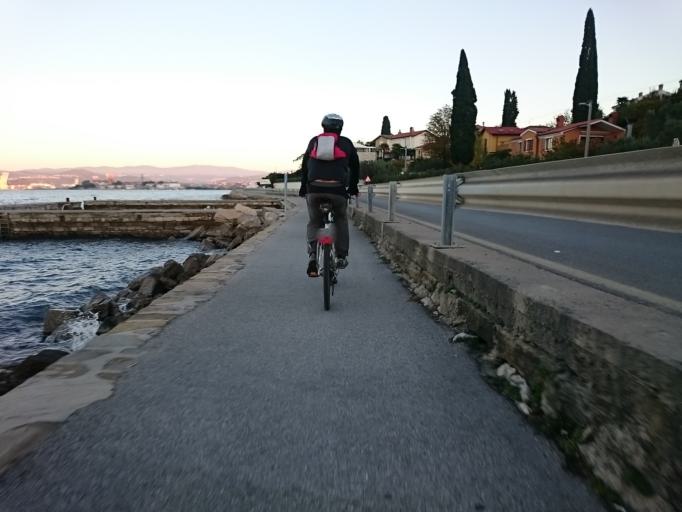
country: SI
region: Koper-Capodistria
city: Koper
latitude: 45.5473
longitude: 13.7045
